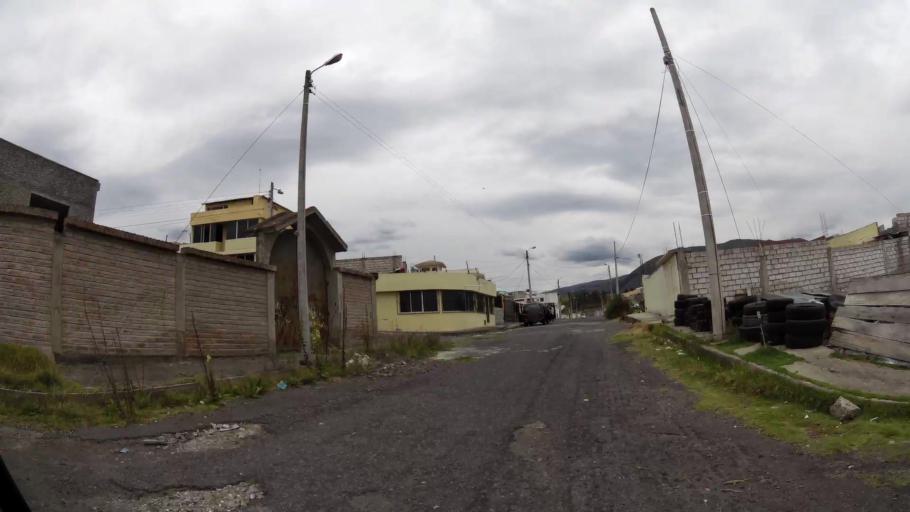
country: EC
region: Cotopaxi
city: Latacunga
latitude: -0.9680
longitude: -78.6149
